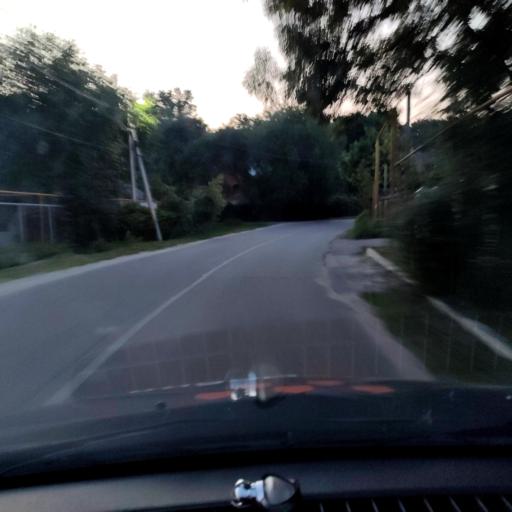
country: RU
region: Voronezj
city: Ramon'
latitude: 51.8197
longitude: 39.2660
